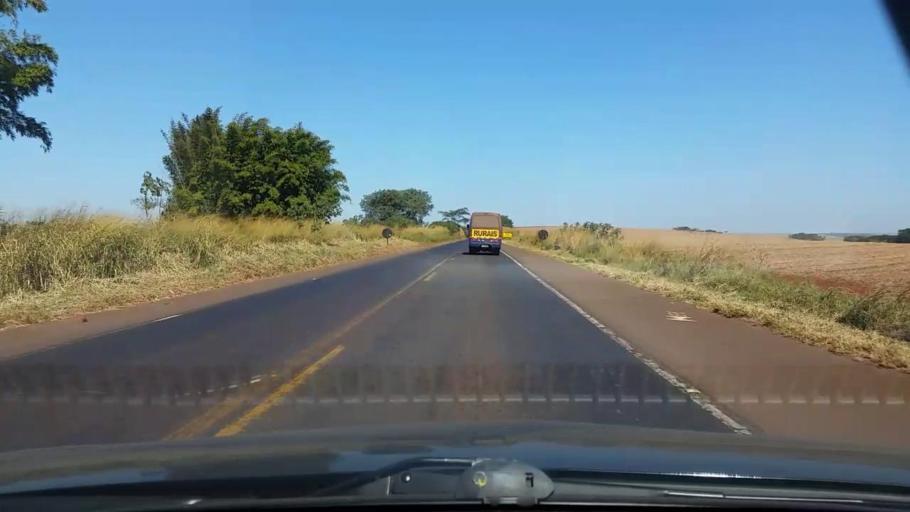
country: BR
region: Sao Paulo
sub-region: Igaracu Do Tiete
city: Igaracu do Tiete
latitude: -22.5665
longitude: -48.5638
